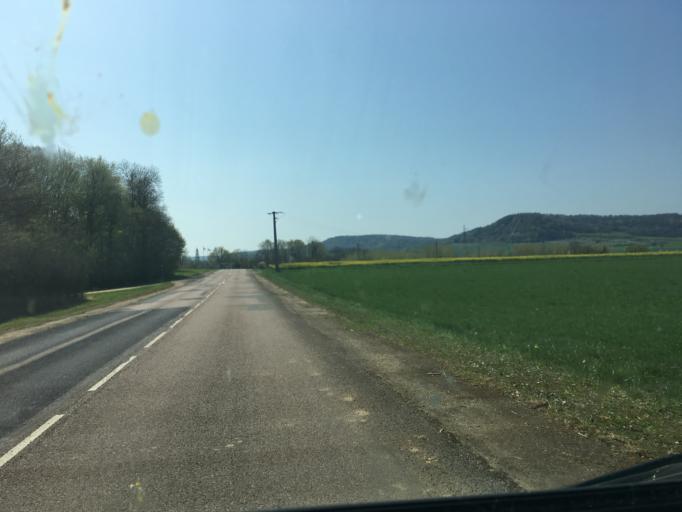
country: FR
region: Lorraine
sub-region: Departement de la Meuse
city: Vigneulles-les-Hattonchatel
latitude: 48.9437
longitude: 5.7187
